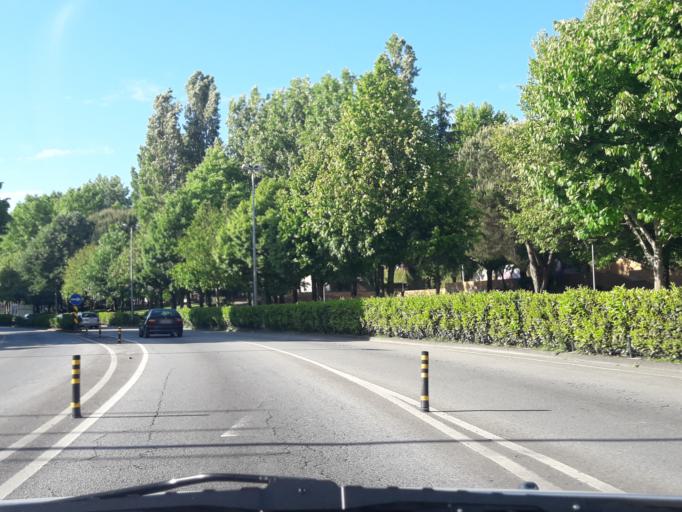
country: PT
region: Braga
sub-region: Vila Nova de Famalicao
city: Vila Nova de Famalicao
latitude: 41.4110
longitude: -8.5168
